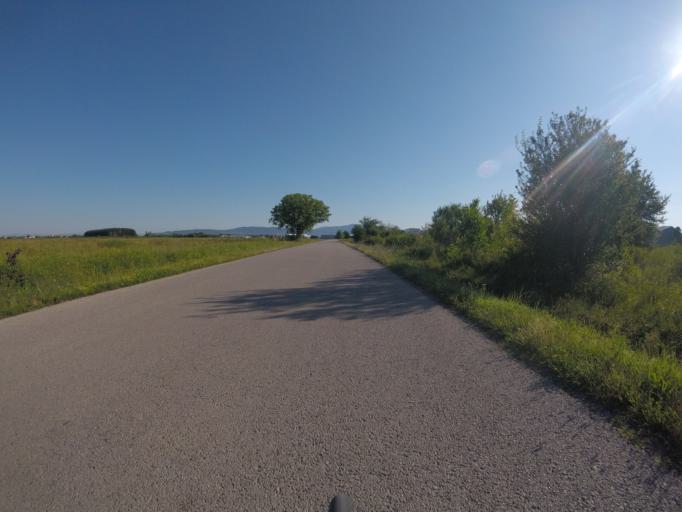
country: HR
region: Grad Zagreb
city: Lucko
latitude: 45.7481
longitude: 15.8724
